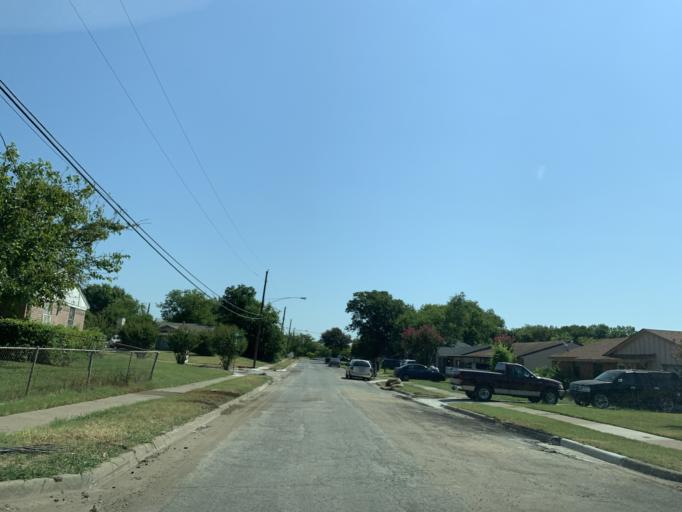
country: US
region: Texas
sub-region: Dallas County
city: Hutchins
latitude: 32.6607
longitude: -96.7554
